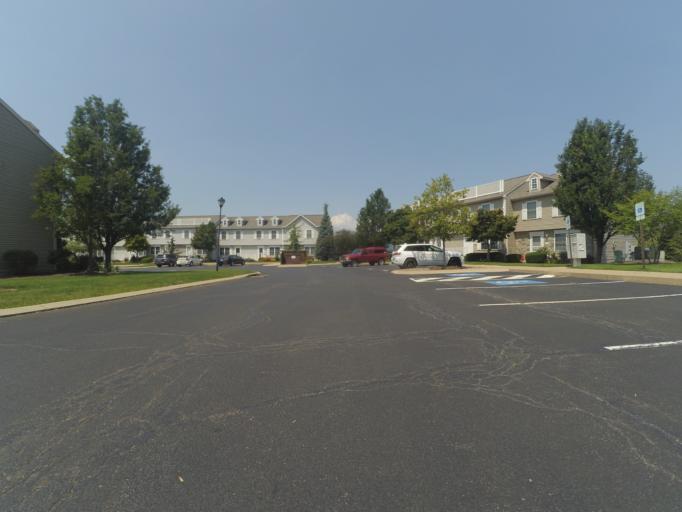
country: US
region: Pennsylvania
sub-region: Centre County
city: Houserville
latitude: 40.8307
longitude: -77.8108
